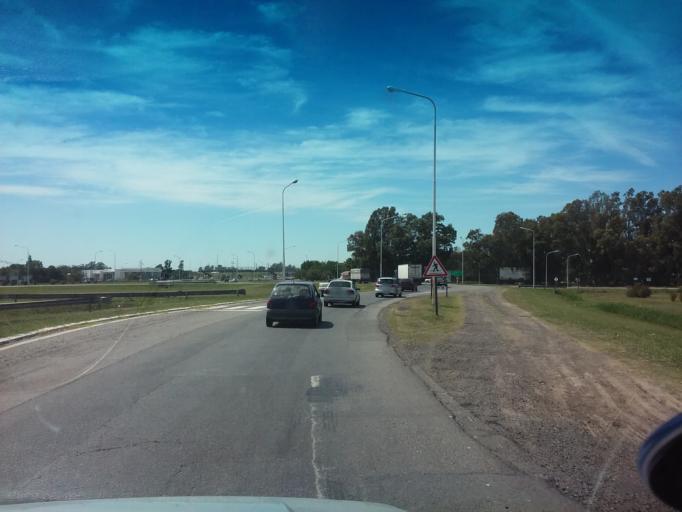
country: AR
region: Buenos Aires
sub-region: Partido de Mercedes
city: Mercedes
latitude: -34.6675
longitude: -59.4092
